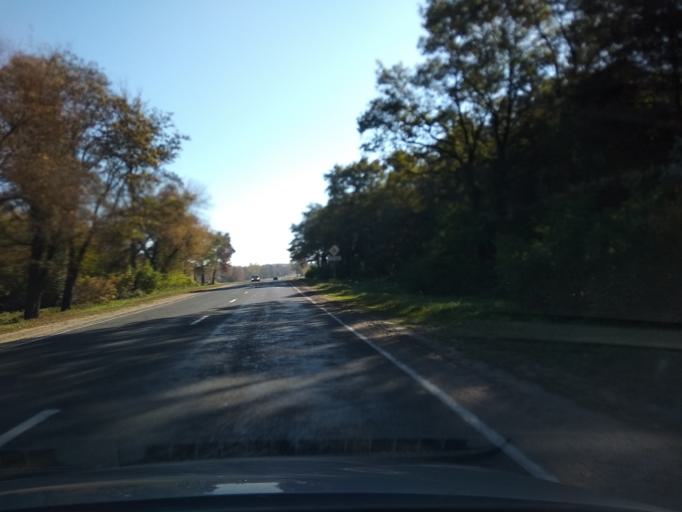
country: BY
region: Brest
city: Malaryta
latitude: 51.9295
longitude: 24.0636
